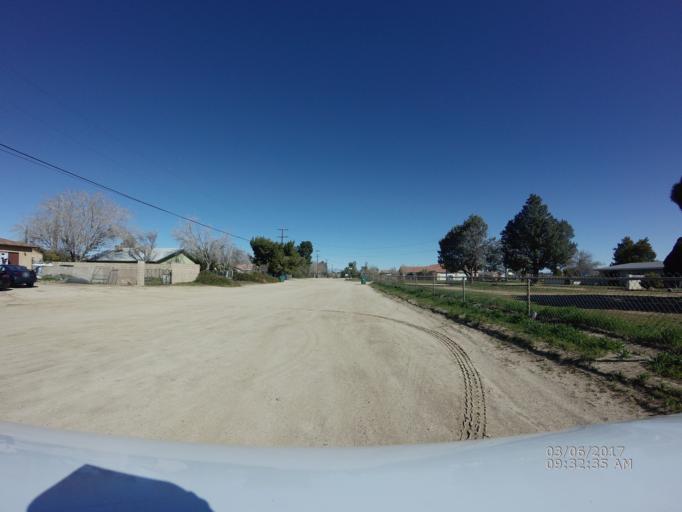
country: US
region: California
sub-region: Los Angeles County
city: Quartz Hill
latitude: 34.6605
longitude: -118.2144
